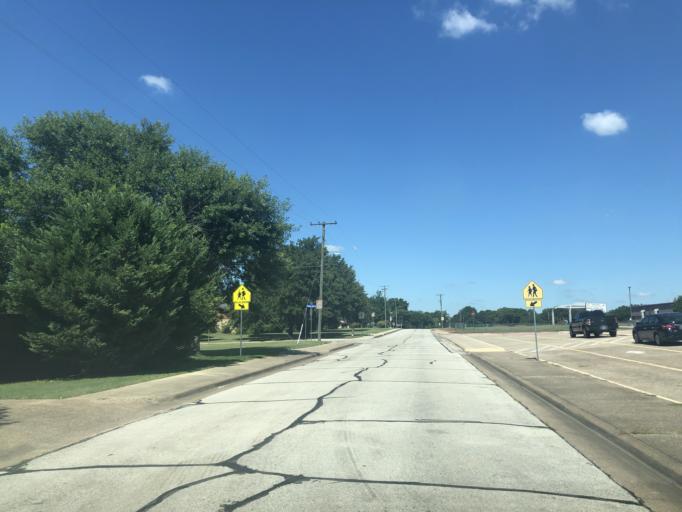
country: US
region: Texas
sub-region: Dallas County
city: Duncanville
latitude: 32.6403
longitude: -96.9309
